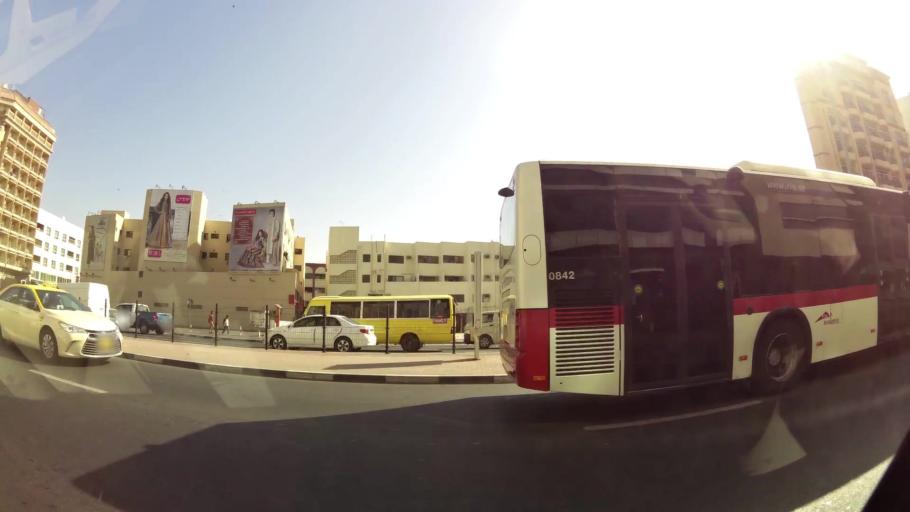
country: AE
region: Ash Shariqah
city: Sharjah
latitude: 25.2593
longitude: 55.2956
